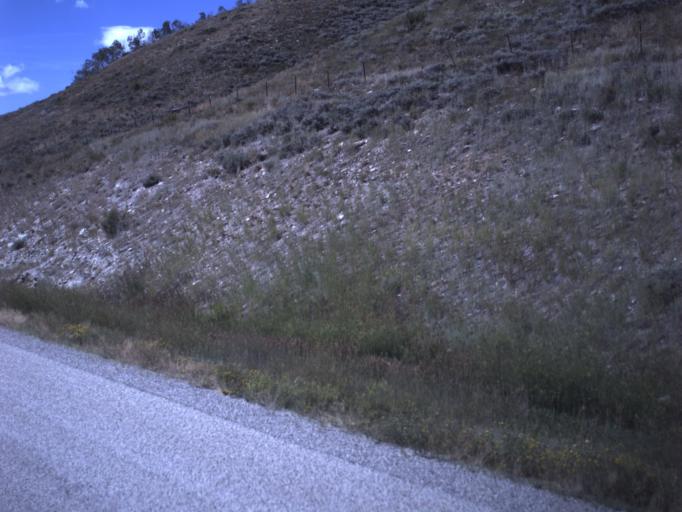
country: US
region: Utah
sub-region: Wasatch County
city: Heber
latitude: 40.2593
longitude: -111.2044
